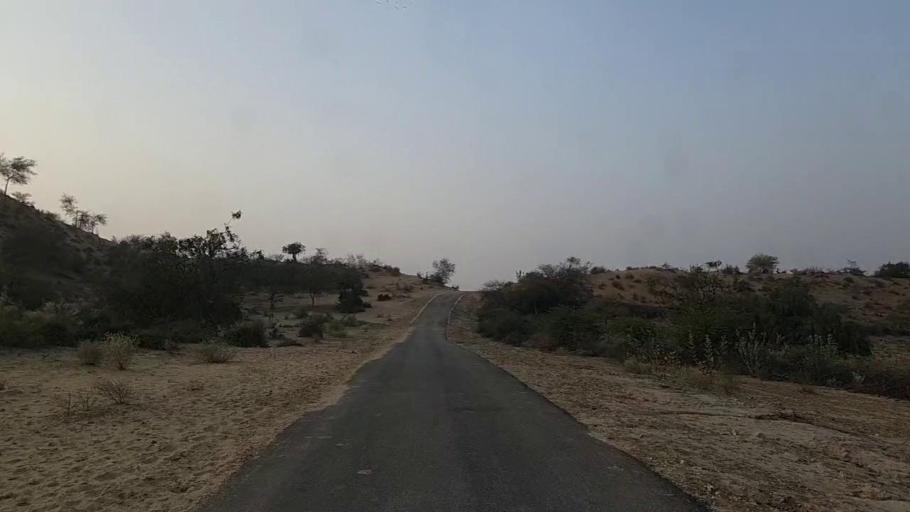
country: PK
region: Sindh
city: Naukot
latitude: 24.6772
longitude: 69.4598
